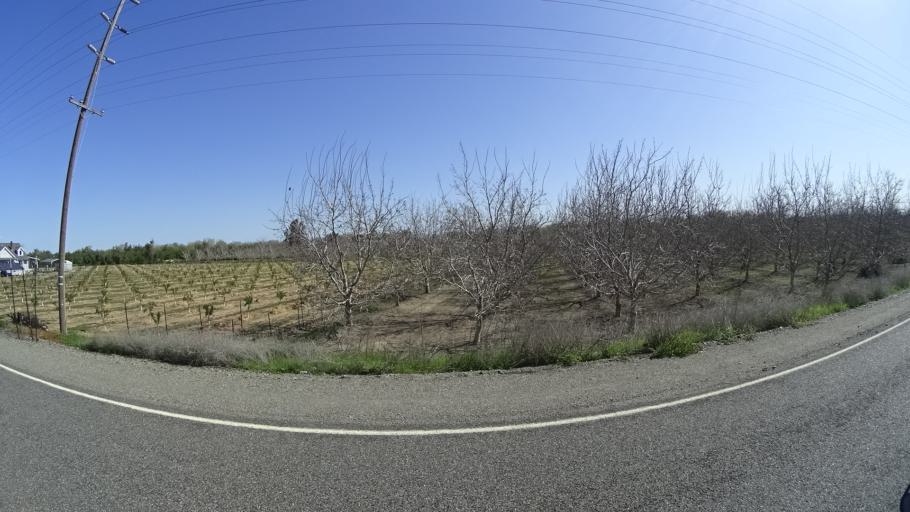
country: US
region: California
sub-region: Glenn County
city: Hamilton City
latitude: 39.7736
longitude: -122.0370
